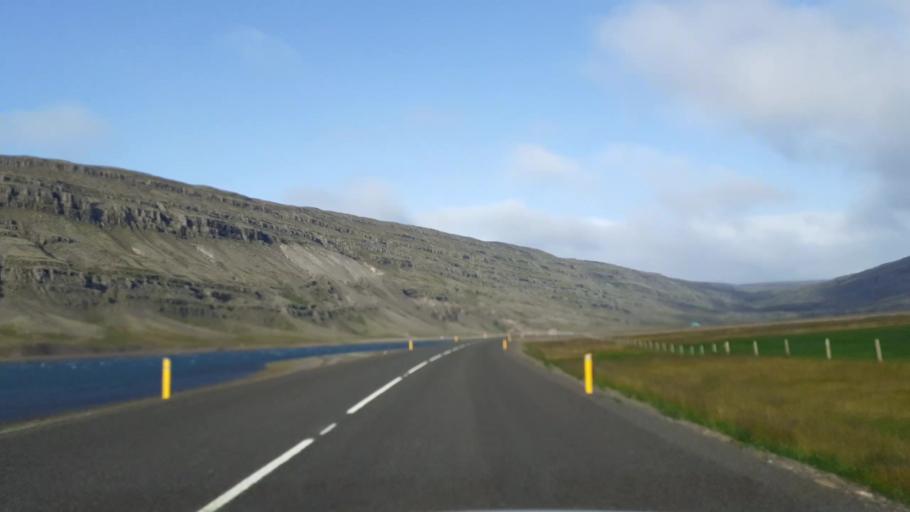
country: IS
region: East
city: Reydarfjoerdur
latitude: 64.7884
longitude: -14.4632
